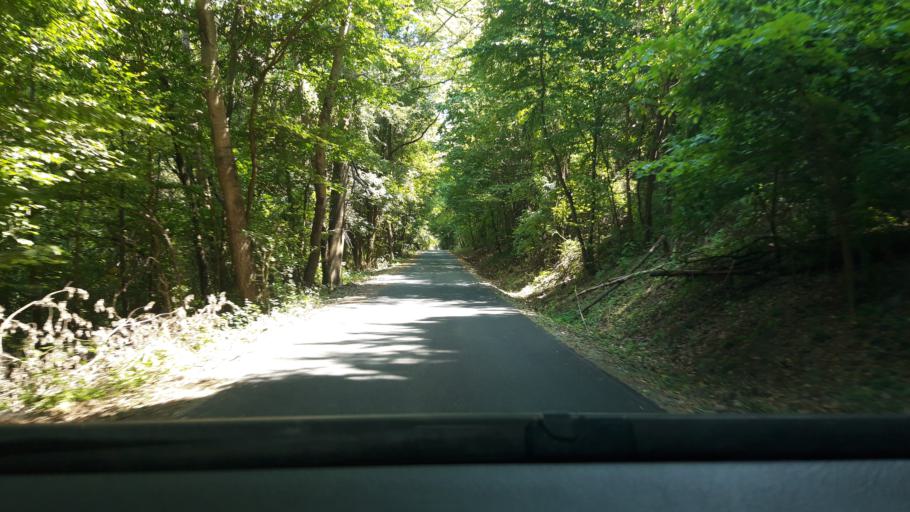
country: HU
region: Nograd
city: Somoskoujfalu
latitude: 48.1809
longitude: 19.8511
